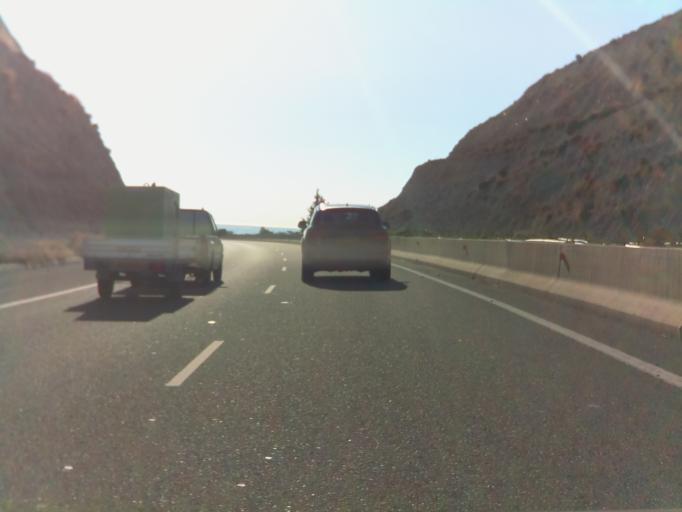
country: CY
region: Limassol
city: Sotira
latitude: 34.6949
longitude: 32.8629
